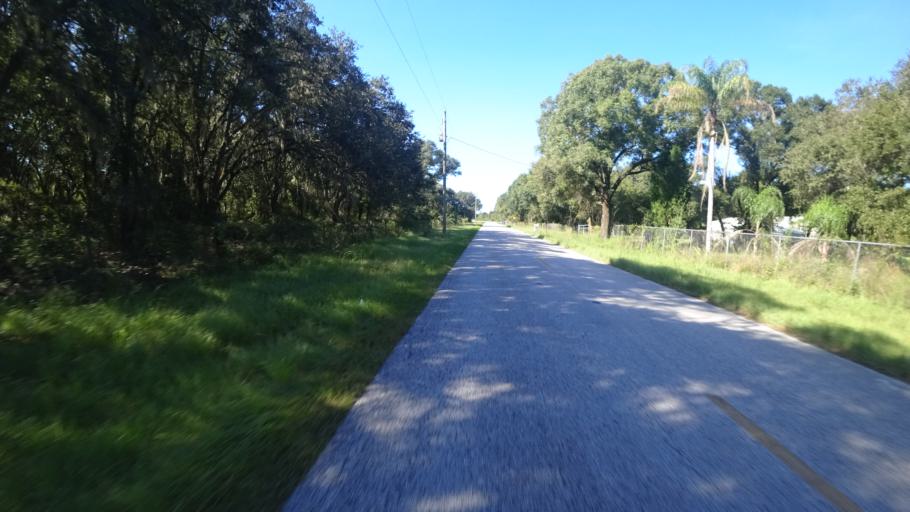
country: US
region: Florida
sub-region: Hillsborough County
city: Wimauma
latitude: 27.6628
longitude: -82.3070
